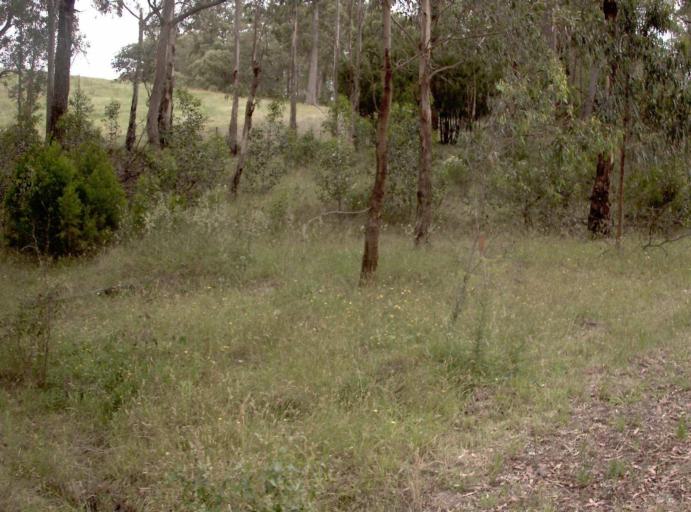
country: AU
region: Victoria
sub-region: East Gippsland
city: Bairnsdale
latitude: -37.7205
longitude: 147.5929
